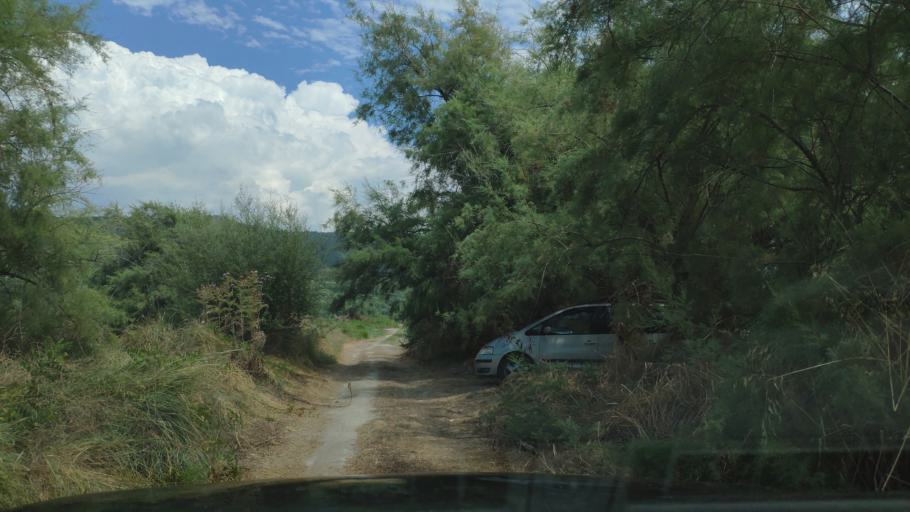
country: GR
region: West Greece
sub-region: Nomos Aitolias kai Akarnanias
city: Menidi
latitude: 39.0485
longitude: 21.0972
